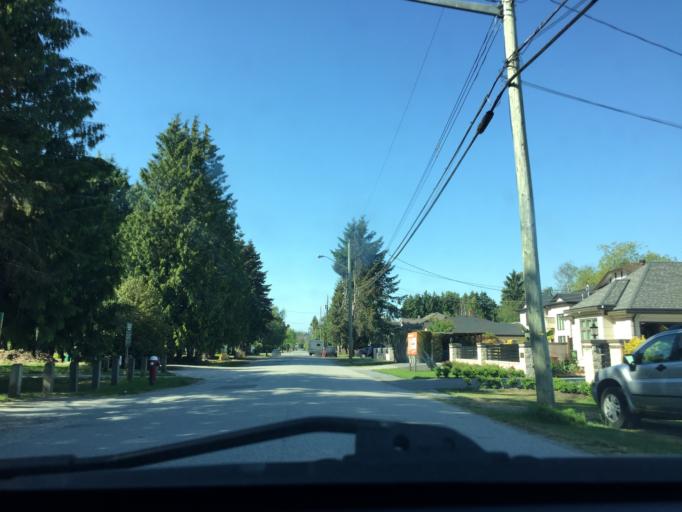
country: CA
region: British Columbia
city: Richmond
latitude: 49.1574
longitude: -123.1198
